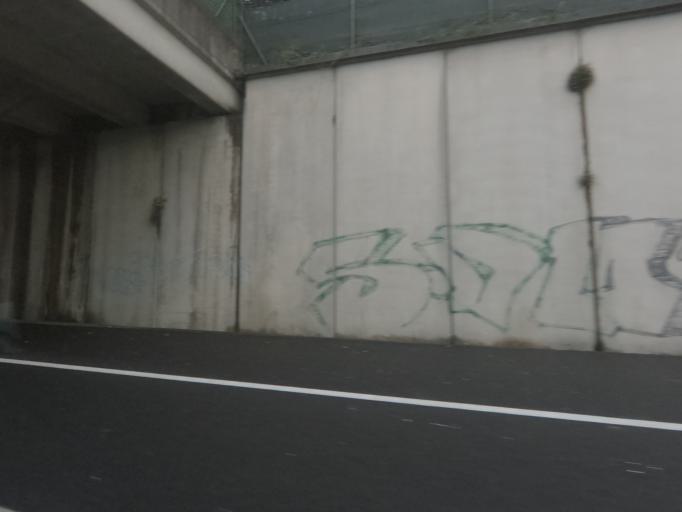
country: ES
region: Galicia
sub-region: Provincia de Pontevedra
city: Redondela
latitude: 42.2291
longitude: -8.6451
